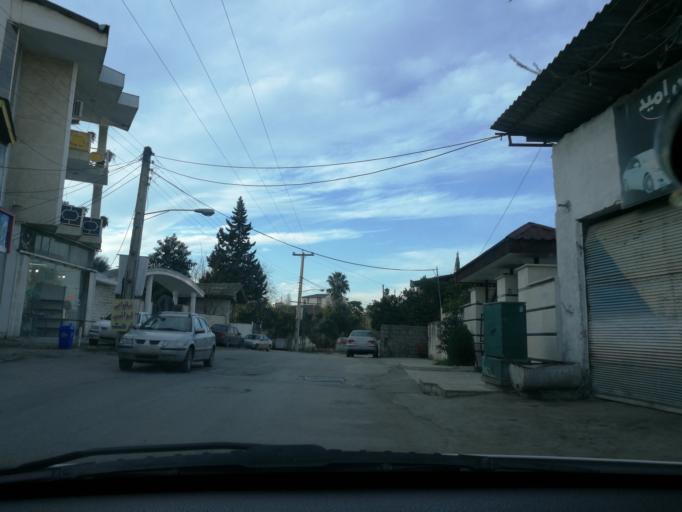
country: IR
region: Mazandaran
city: Chalus
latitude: 36.6467
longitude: 51.4303
